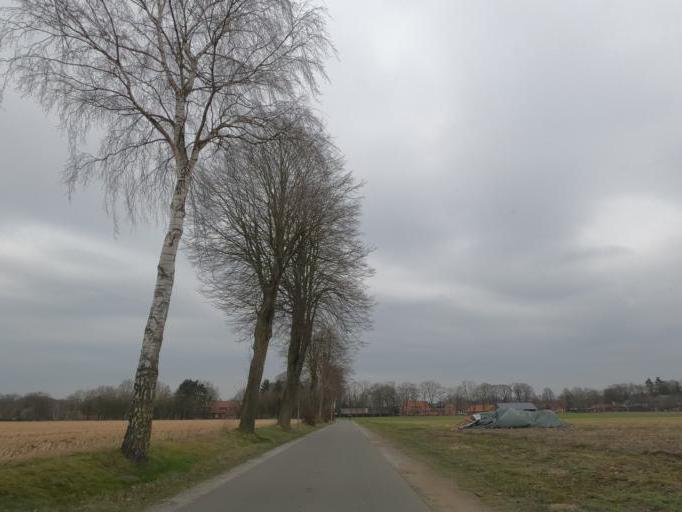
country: DE
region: Lower Saxony
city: Molbergen
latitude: 52.8785
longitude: 7.9076
